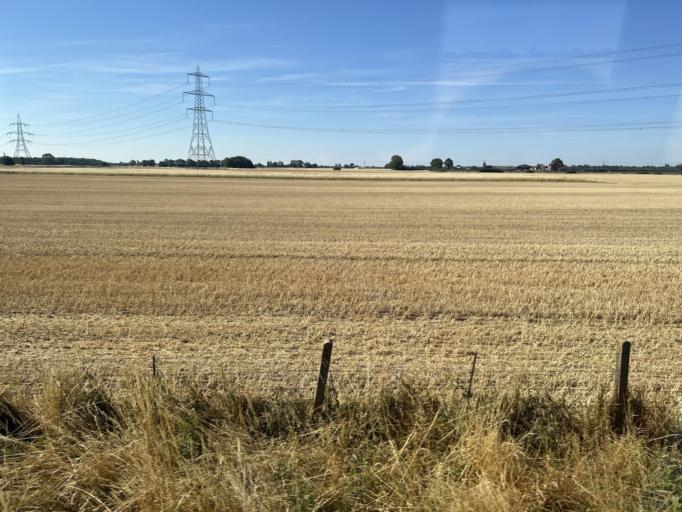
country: GB
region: England
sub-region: Lincolnshire
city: Heckington
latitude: 52.9725
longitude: -0.2676
